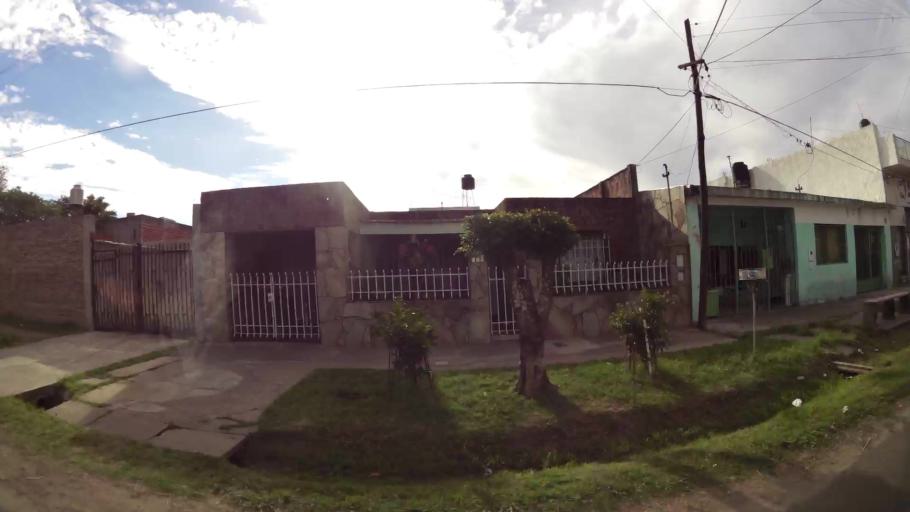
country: AR
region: Santa Fe
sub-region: Departamento de Rosario
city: Rosario
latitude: -32.9753
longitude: -60.6855
